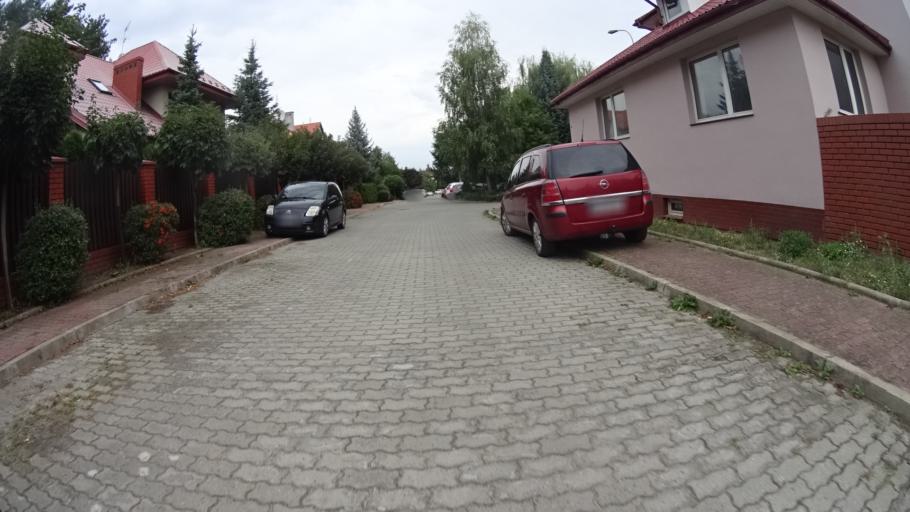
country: PL
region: Masovian Voivodeship
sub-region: Powiat pruszkowski
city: Nadarzyn
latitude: 52.1063
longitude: 20.7975
